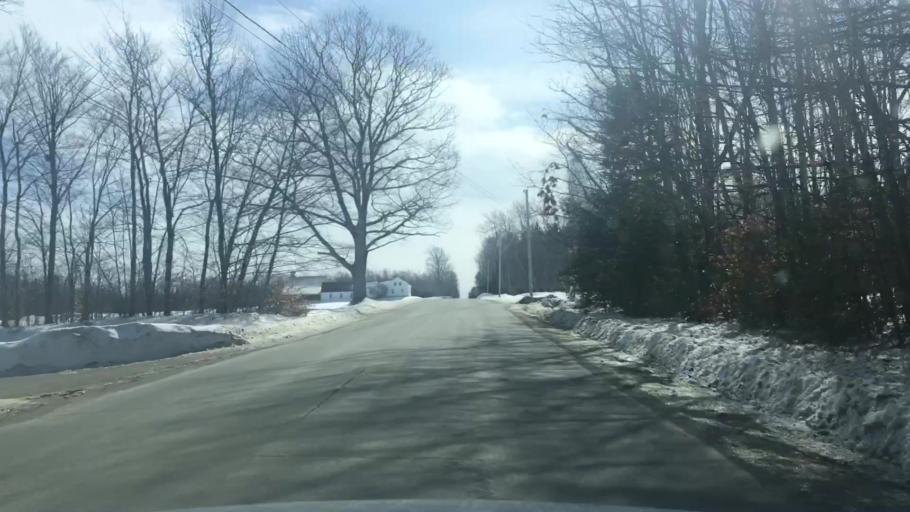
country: US
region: Maine
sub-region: Penobscot County
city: Holden
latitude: 44.7763
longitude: -68.6511
